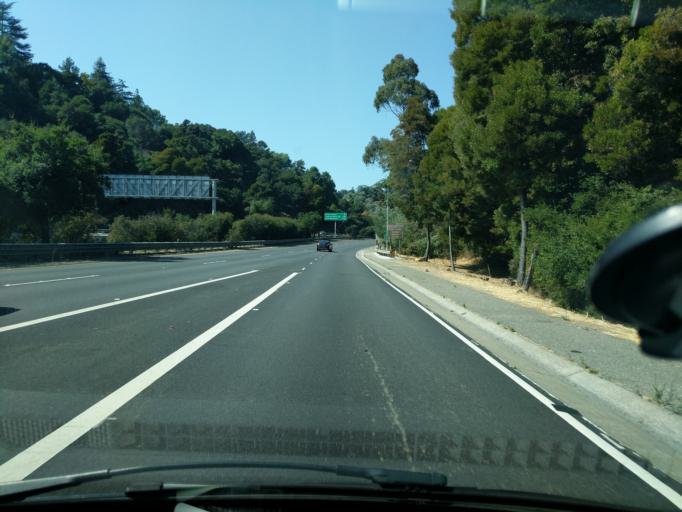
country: US
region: California
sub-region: Alameda County
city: Piedmont
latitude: 37.7868
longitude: -122.1798
